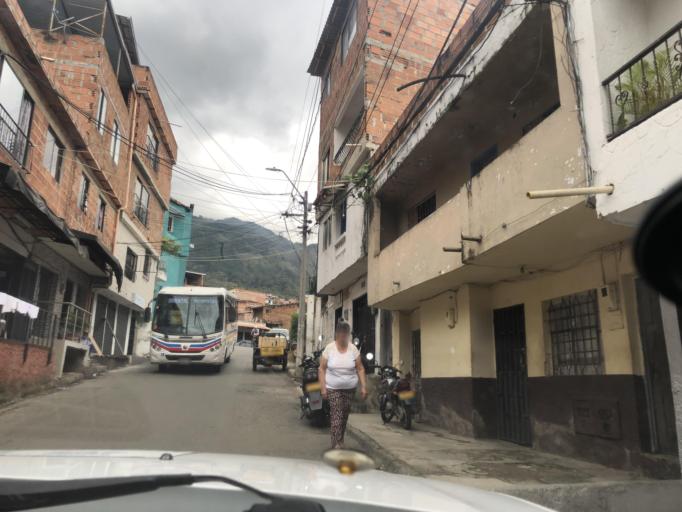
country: CO
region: Antioquia
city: Bello
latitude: 6.3467
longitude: -75.5635
